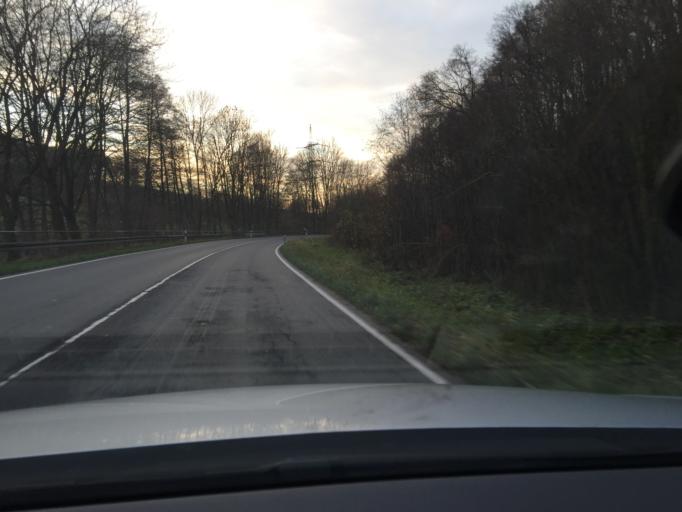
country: DE
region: North Rhine-Westphalia
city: Hattingen
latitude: 51.3717
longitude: 7.1715
